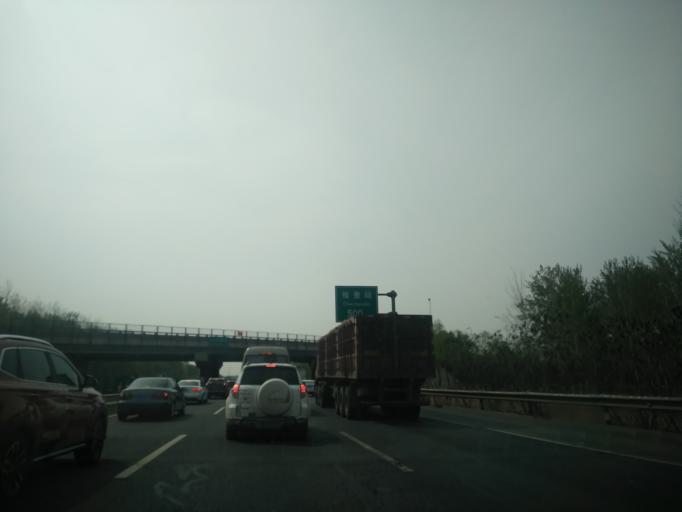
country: CN
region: Beijing
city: Xiji
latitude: 39.7989
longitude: 116.9070
